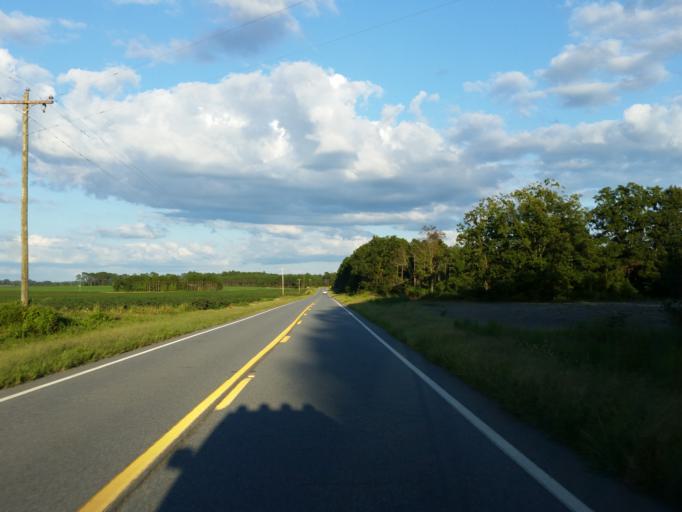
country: US
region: Georgia
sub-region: Dooly County
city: Vienna
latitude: 32.0862
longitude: -83.7256
